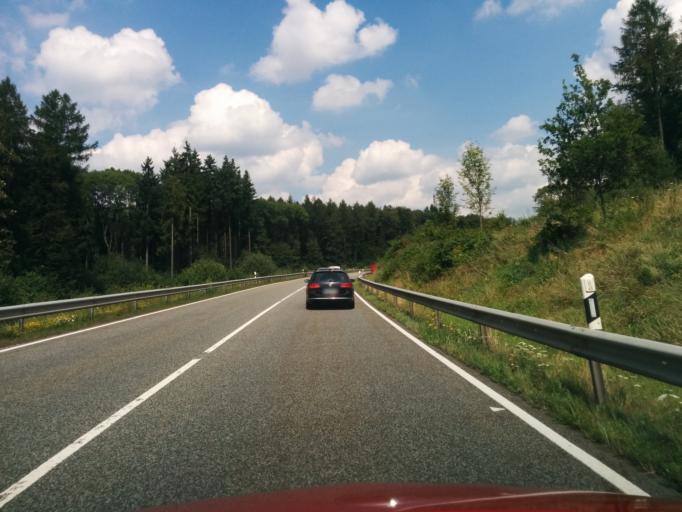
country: DE
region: Rheinland-Pfalz
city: Neuhausel
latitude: 50.3812
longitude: 7.7000
